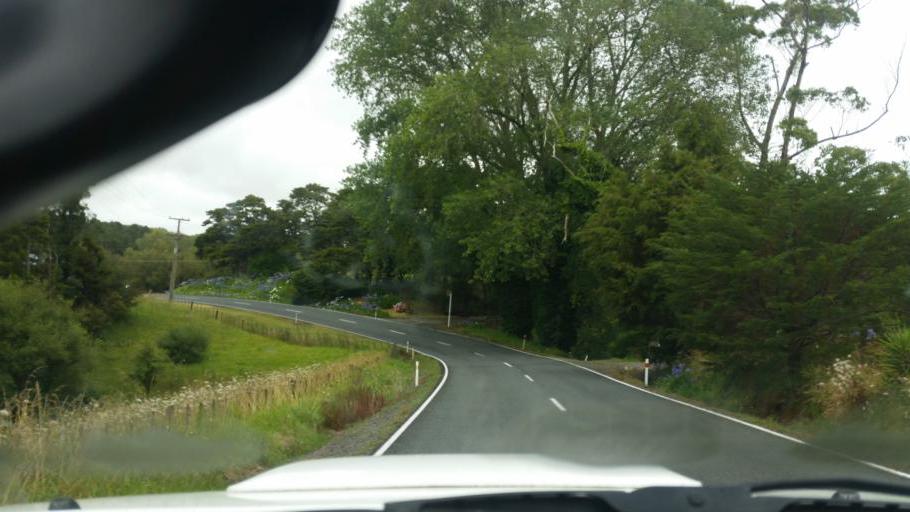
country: NZ
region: Auckland
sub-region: Auckland
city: Wellsford
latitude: -36.1569
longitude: 174.4619
